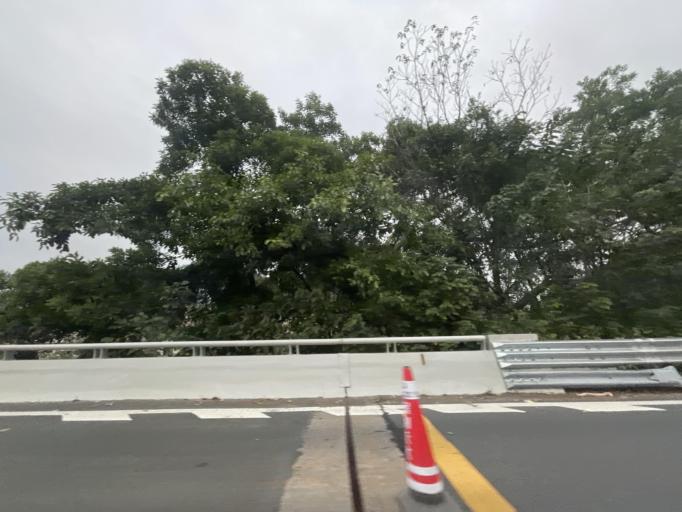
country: CN
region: Guangdong
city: Humen
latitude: 22.8071
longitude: 113.6458
